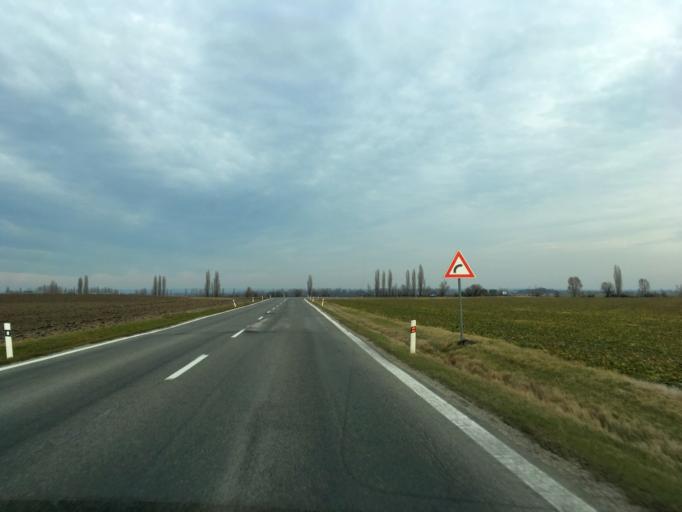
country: SK
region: Nitriansky
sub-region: Okres Nove Zamky
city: Nove Zamky
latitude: 47.9909
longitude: 18.2213
